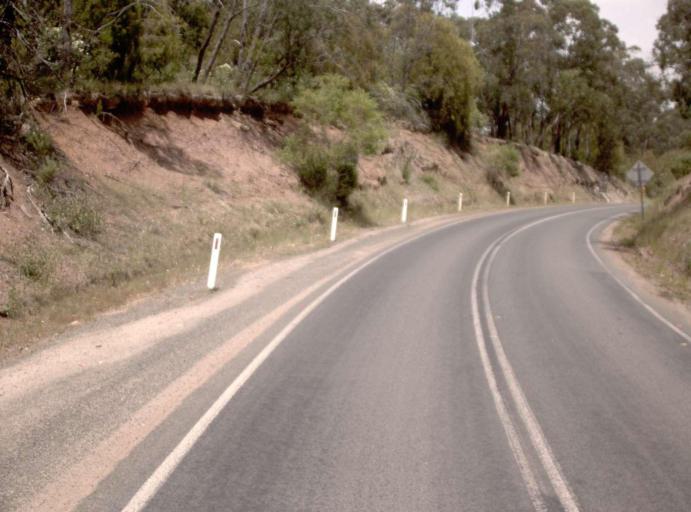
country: AU
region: Victoria
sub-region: Latrobe
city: Traralgon
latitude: -38.3820
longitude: 146.7587
